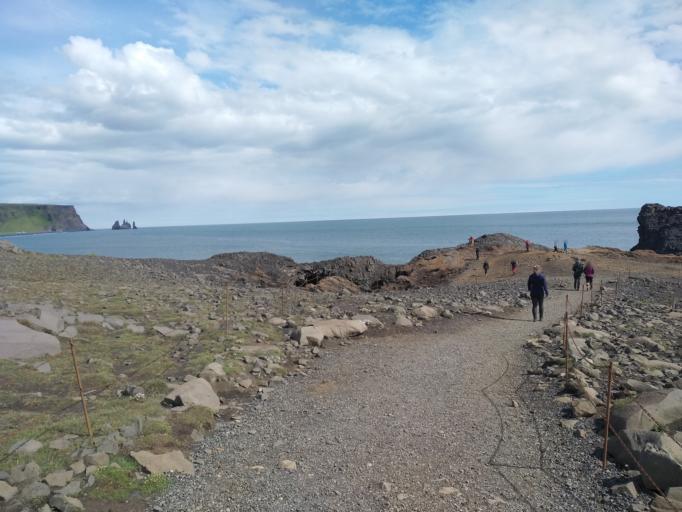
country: IS
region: South
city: Vestmannaeyjar
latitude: 63.4032
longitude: -19.1038
